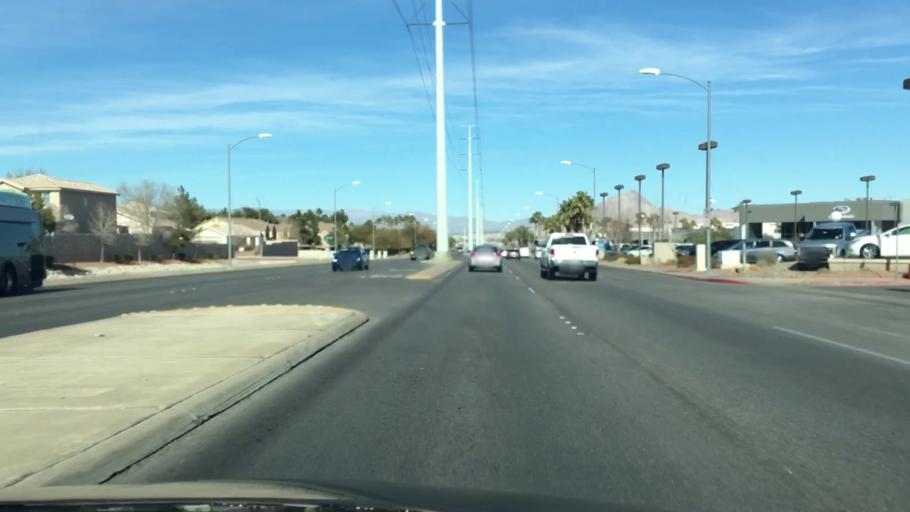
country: US
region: Nevada
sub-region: Clark County
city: Henderson
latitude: 36.0476
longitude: -115.0290
